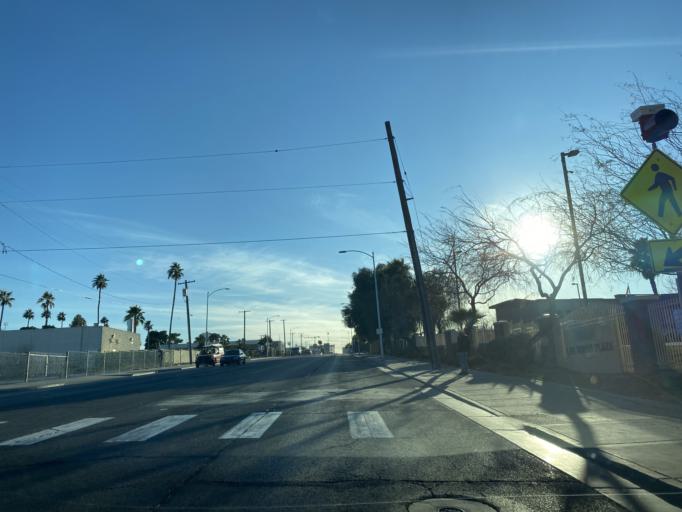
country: US
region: Nevada
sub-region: Clark County
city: Las Vegas
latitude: 36.1870
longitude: -115.1365
